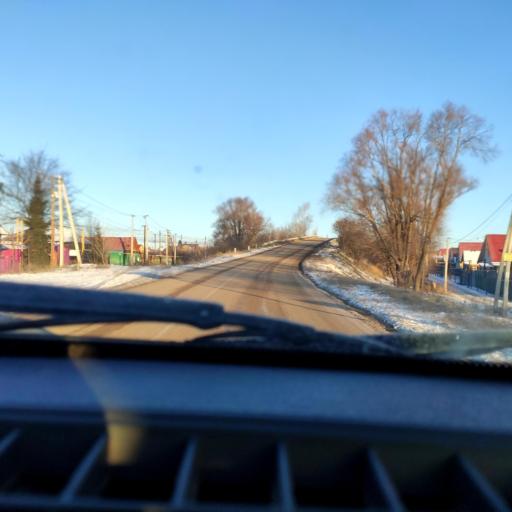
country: RU
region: Bashkortostan
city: Avdon
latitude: 54.6498
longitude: 55.7783
